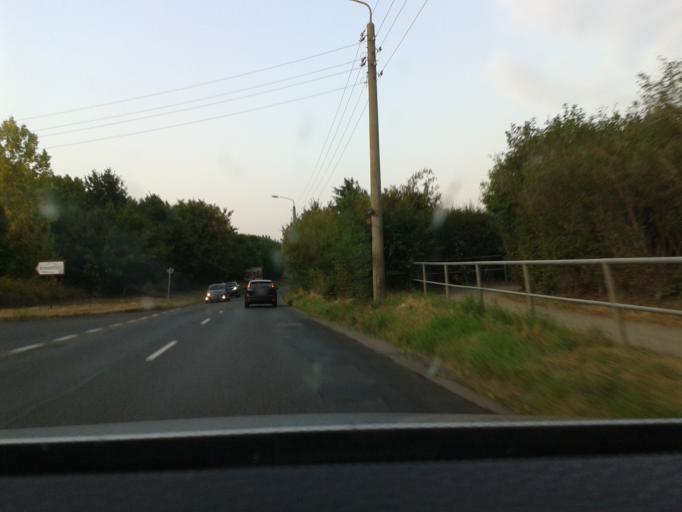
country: DE
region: Saxony
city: Heidenau
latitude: 51.0022
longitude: 13.8035
